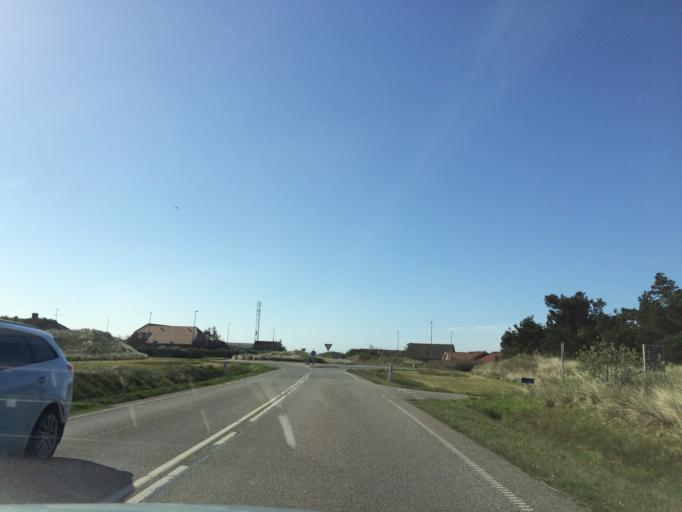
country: DK
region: Central Jutland
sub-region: Ringkobing-Skjern Kommune
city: Hvide Sande
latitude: 56.0216
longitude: 8.1221
